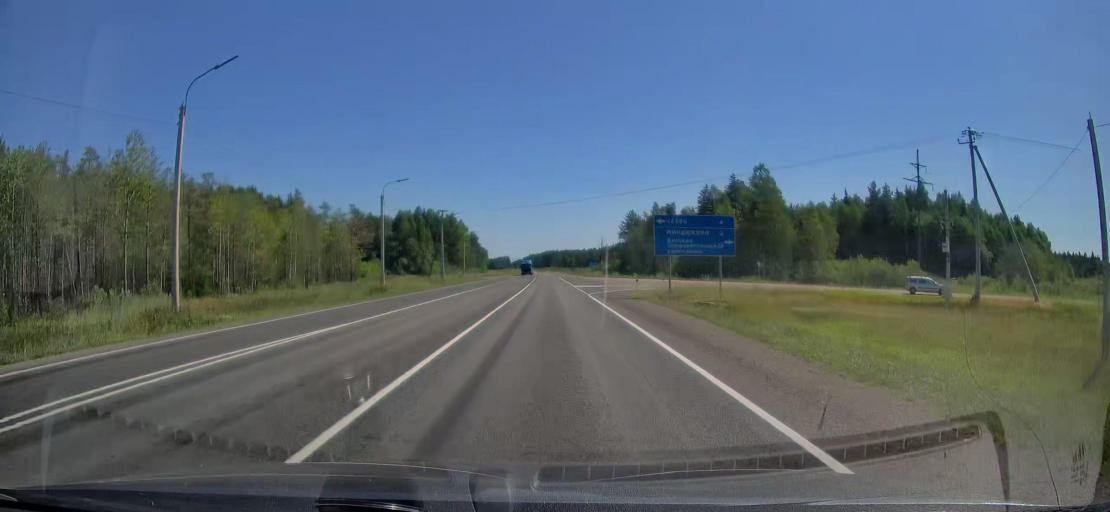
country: RU
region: Tverskaya
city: Ves'yegonsk
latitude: 58.9236
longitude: 37.1824
